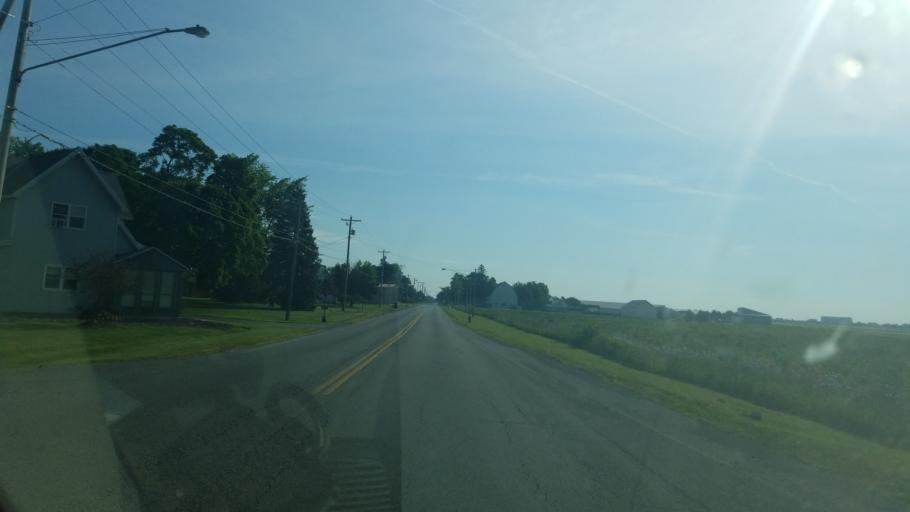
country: US
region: Ohio
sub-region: Hancock County
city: Findlay
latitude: 41.0126
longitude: -83.6840
